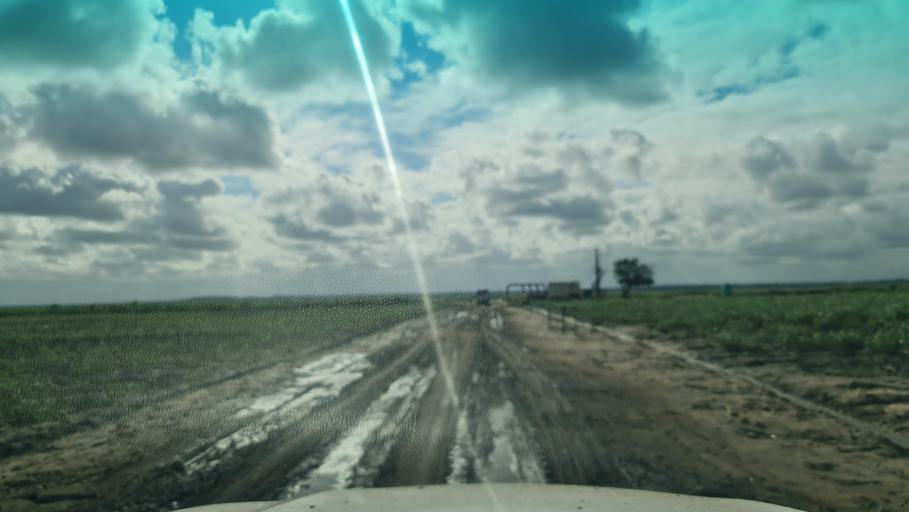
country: MZ
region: Maputo
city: Manhica
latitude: -25.4377
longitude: 32.8422
